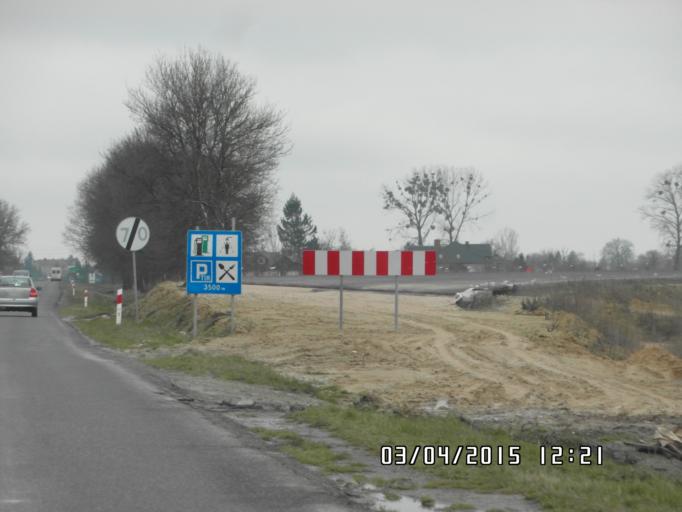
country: PL
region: Lublin Voivodeship
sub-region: Powiat hrubieszowski
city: Hrubieszow
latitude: 50.8287
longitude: 23.9561
